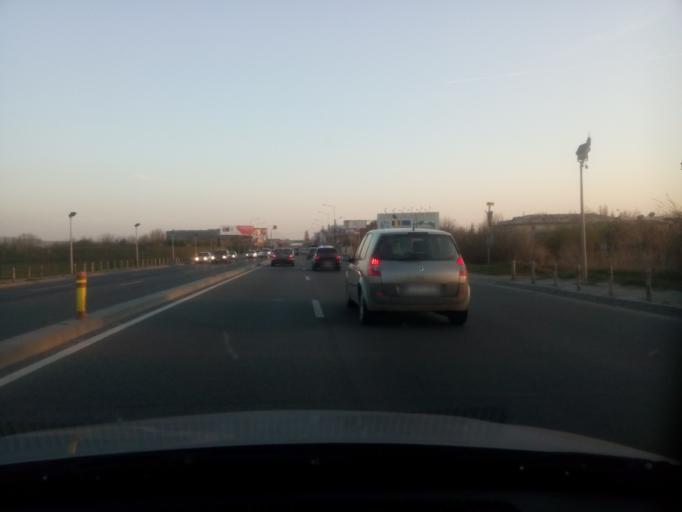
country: RO
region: Ilfov
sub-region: Comuna Otopeni
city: Otopeni
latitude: 44.5643
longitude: 26.0696
